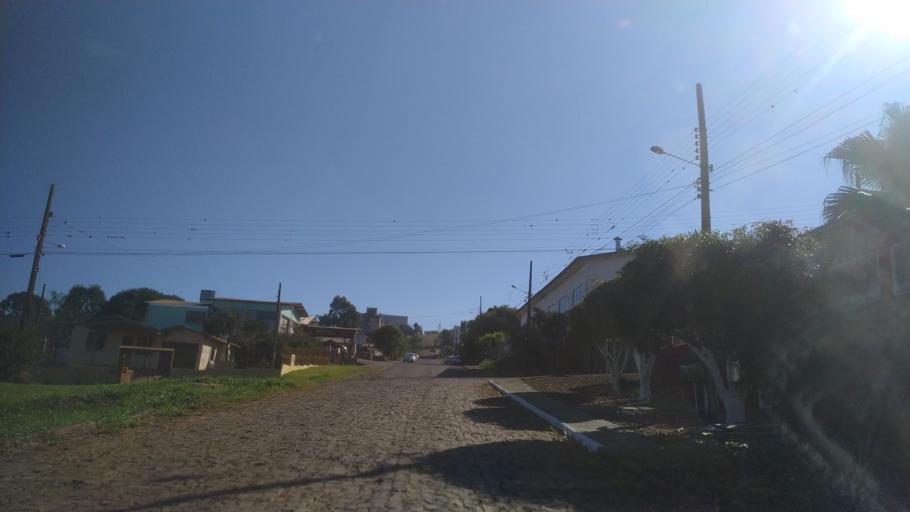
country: BR
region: Santa Catarina
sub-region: Chapeco
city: Chapeco
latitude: -27.1139
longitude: -52.5966
